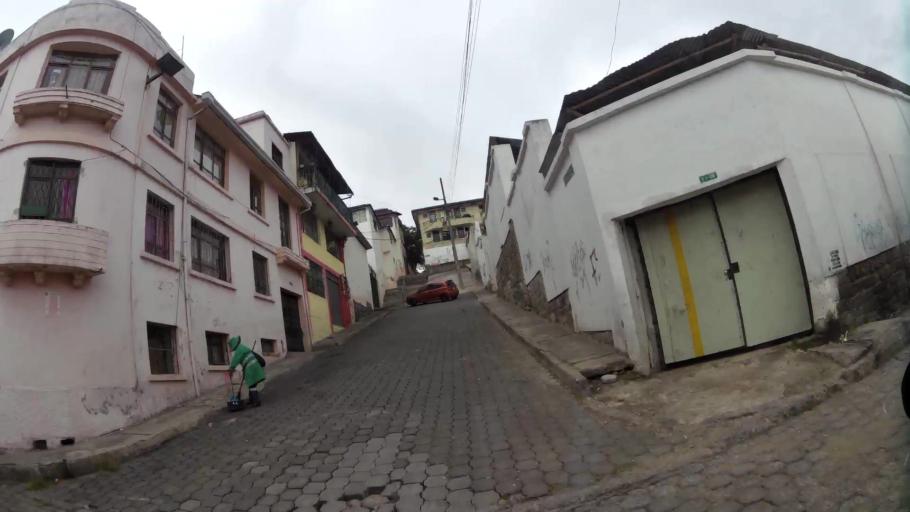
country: EC
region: Pichincha
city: Quito
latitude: -0.2272
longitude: -78.5088
